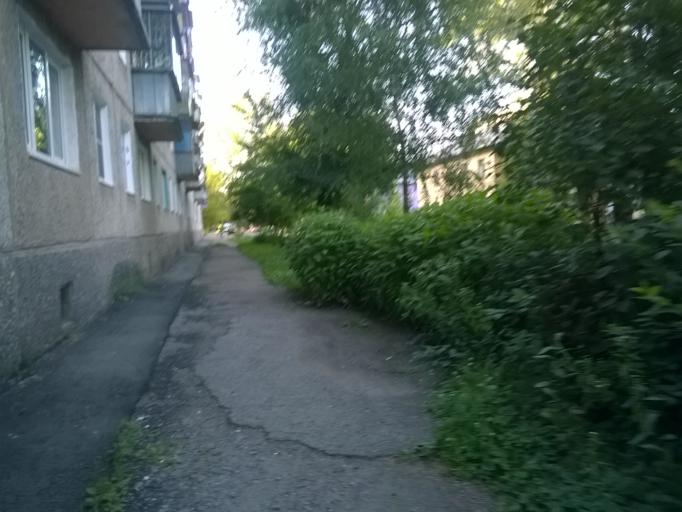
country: RU
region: Kursk
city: Kursk
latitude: 51.6686
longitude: 36.1492
